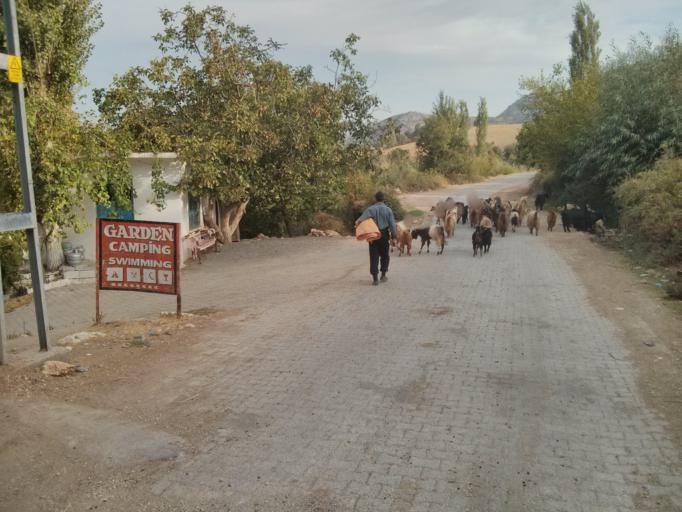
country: TR
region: Adiyaman
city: Damlacik
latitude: 37.9170
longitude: 38.6549
